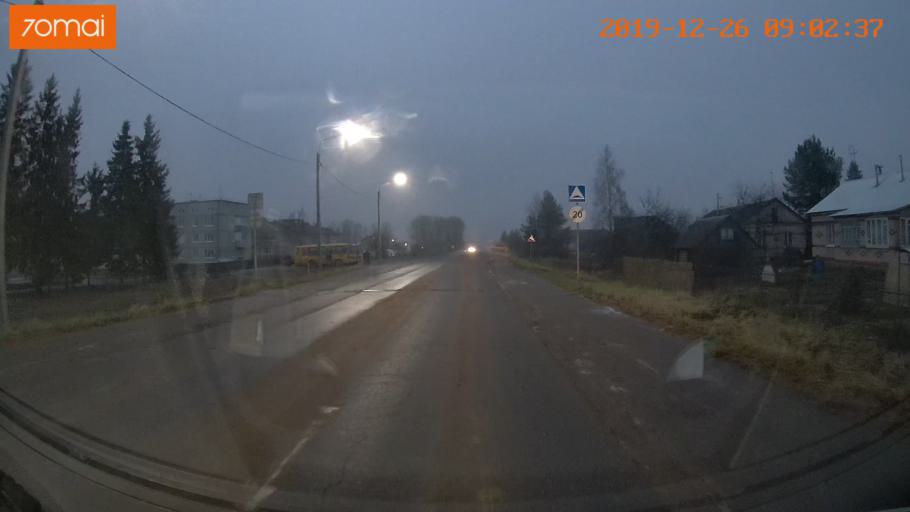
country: RU
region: Vologda
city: Gryazovets
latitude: 58.7970
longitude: 40.2661
